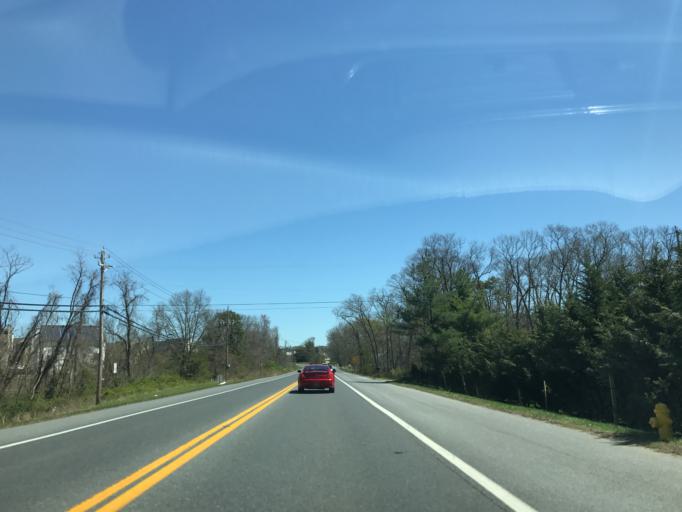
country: US
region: Maryland
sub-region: Anne Arundel County
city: South Gate
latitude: 39.1363
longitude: -76.6613
